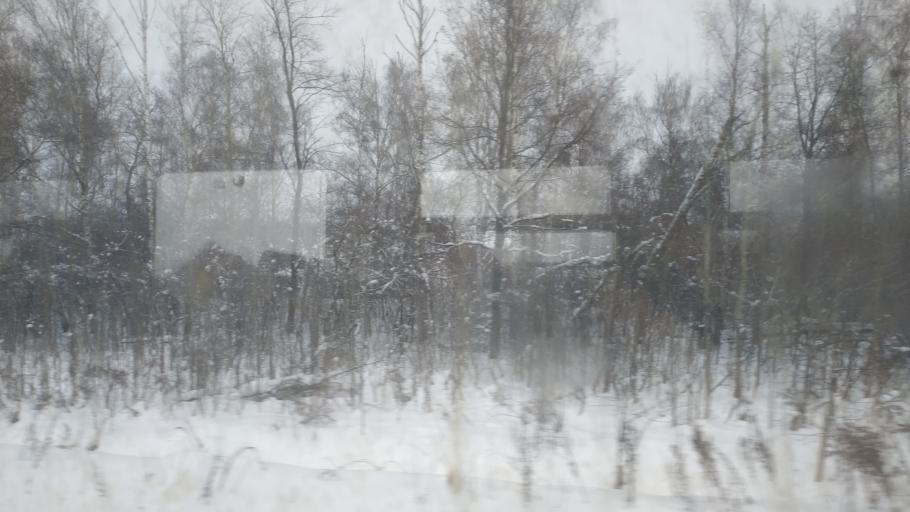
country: RU
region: Moskovskaya
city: Malyshevo
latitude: 55.5379
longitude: 38.3016
